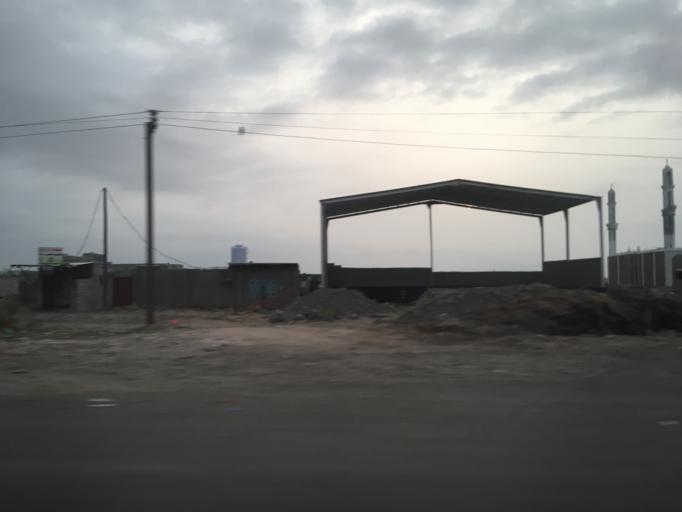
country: YE
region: Lahij
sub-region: Al  Hawtah
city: Lahij
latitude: 13.0241
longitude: 44.8917
